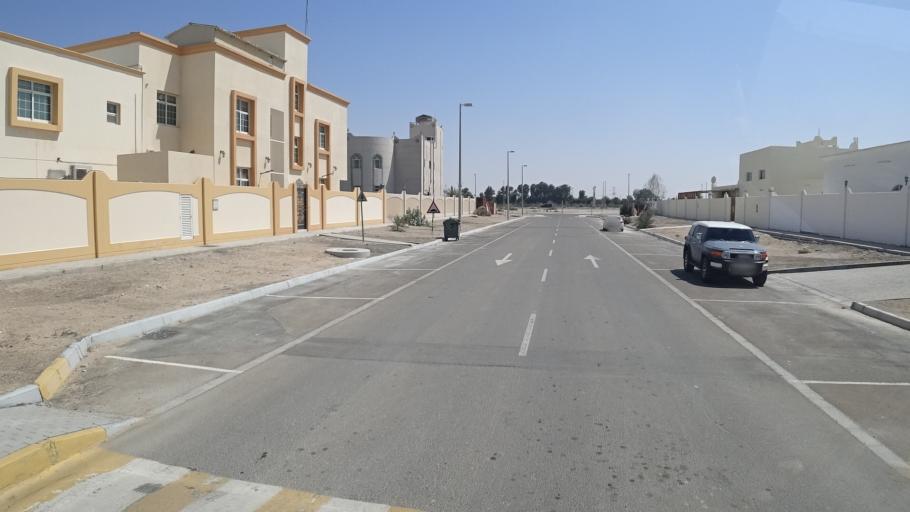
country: AE
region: Abu Dhabi
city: Abu Dhabi
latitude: 24.5450
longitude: 54.6348
